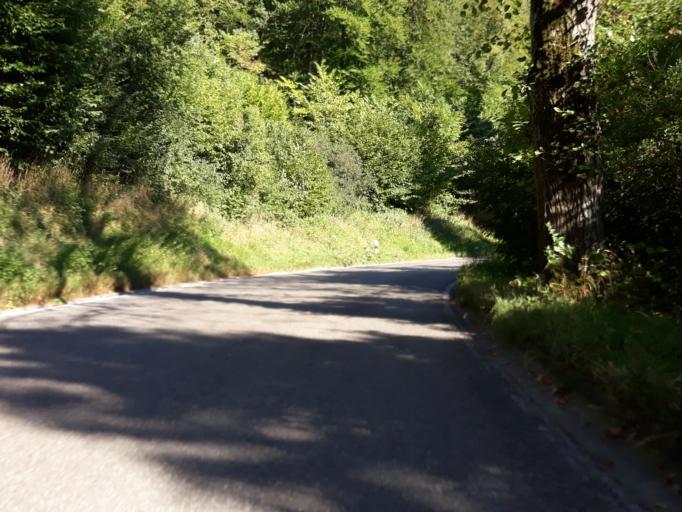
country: DE
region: Baden-Wuerttemberg
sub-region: Regierungsbezirk Stuttgart
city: Aidlingen
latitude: 48.6676
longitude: 8.9166
